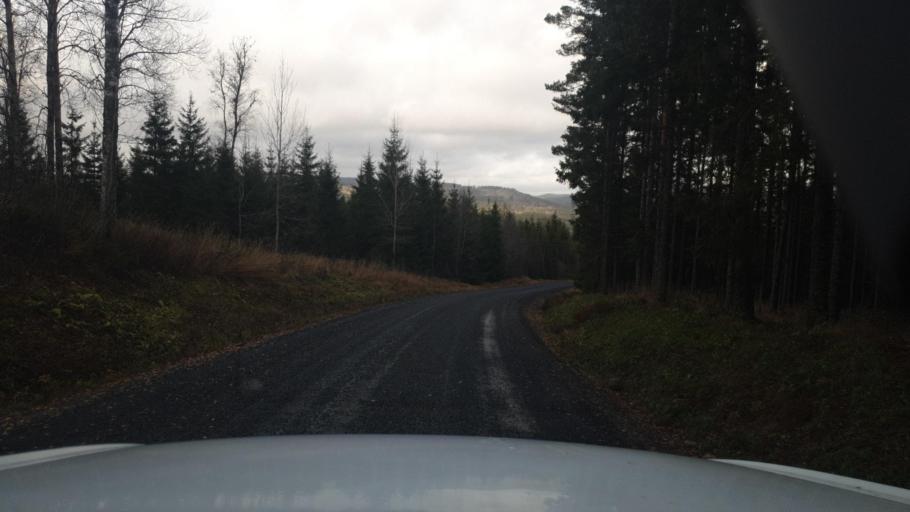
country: SE
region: Vaermland
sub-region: Torsby Kommun
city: Torsby
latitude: 60.1843
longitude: 12.6444
